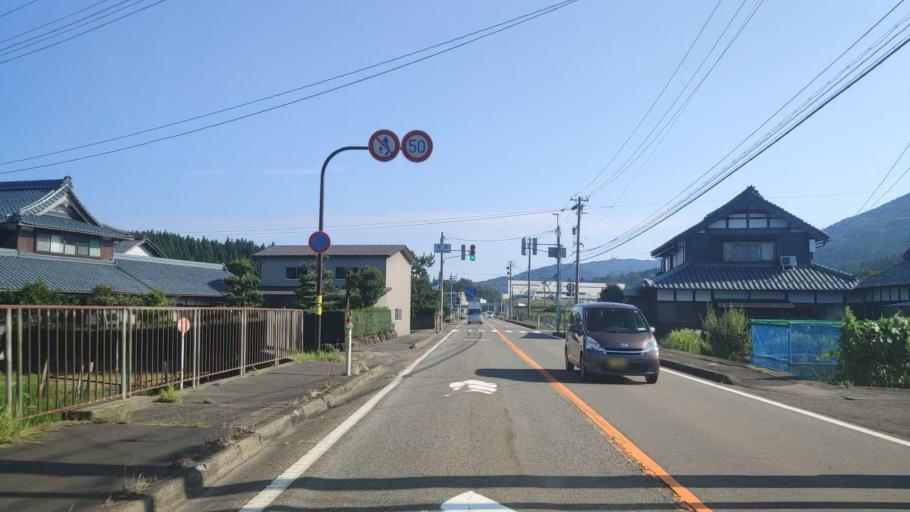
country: JP
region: Fukui
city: Maruoka
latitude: 36.2334
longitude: 136.2867
